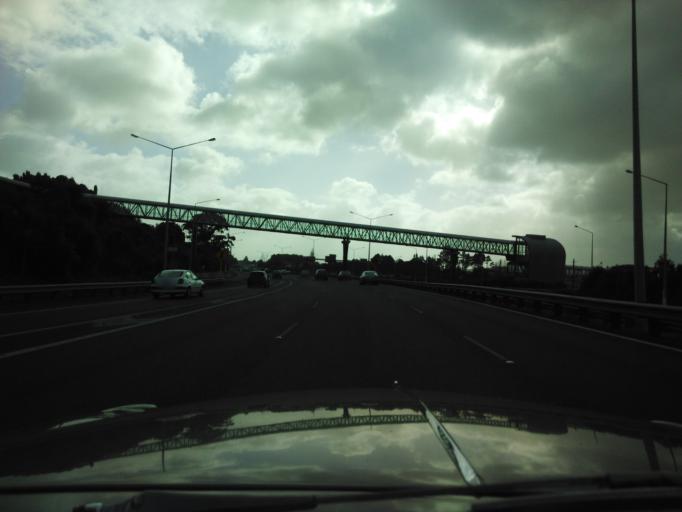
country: NZ
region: Auckland
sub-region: Auckland
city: North Shore
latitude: -36.7986
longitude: 174.7609
